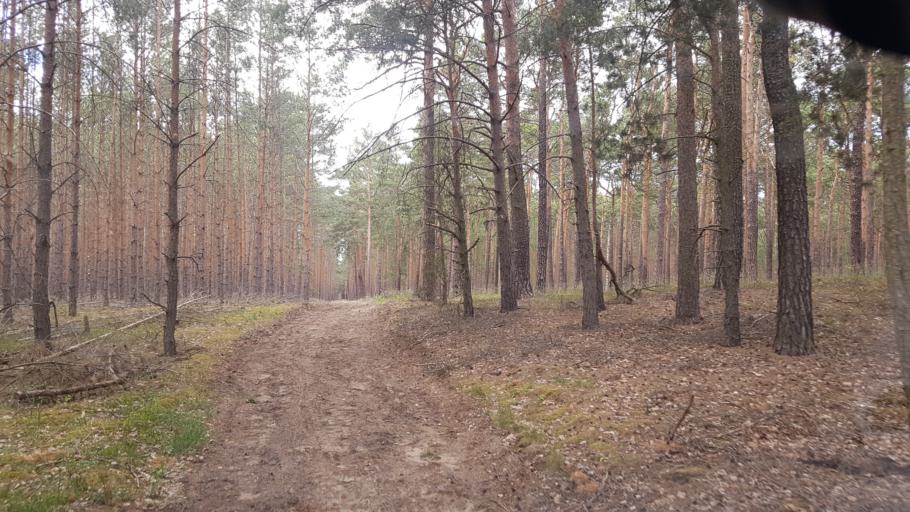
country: DE
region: Brandenburg
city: Finsterwalde
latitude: 51.6183
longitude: 13.6595
